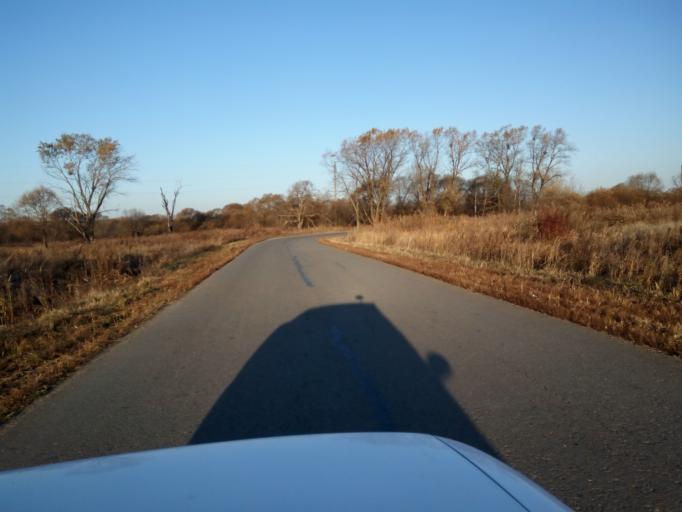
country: RU
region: Primorskiy
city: Lazo
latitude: 45.8586
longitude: 133.6407
